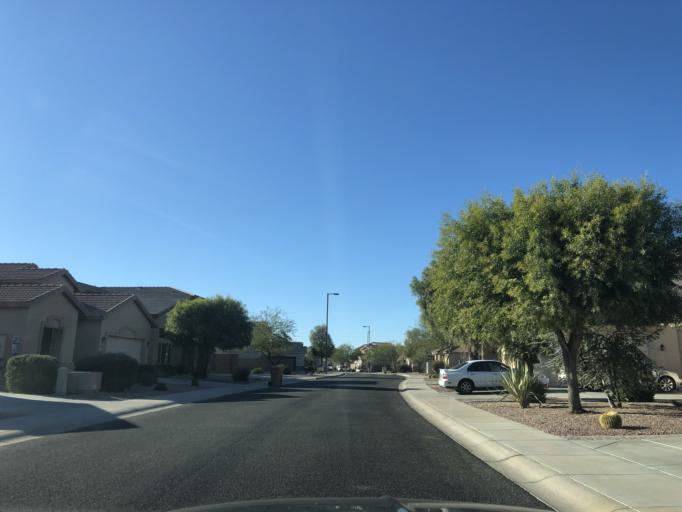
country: US
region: Arizona
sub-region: Maricopa County
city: Buckeye
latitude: 33.4245
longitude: -112.6057
